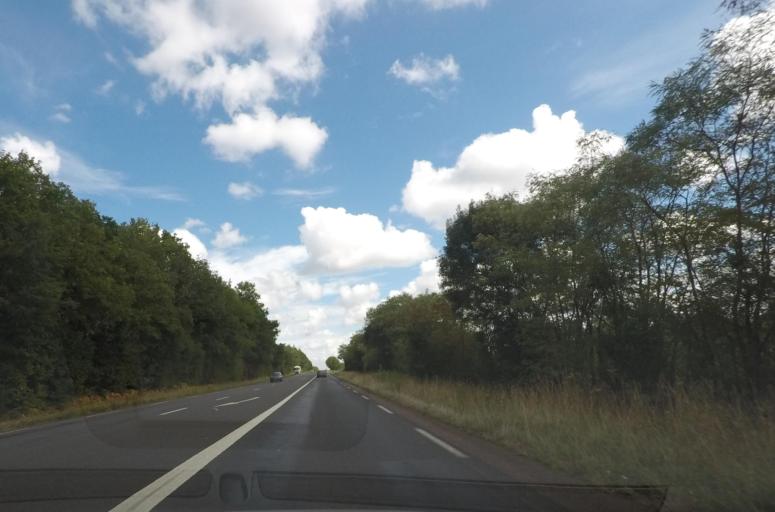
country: FR
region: Pays de la Loire
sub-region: Departement de la Sarthe
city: Clermont-Creans
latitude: 47.7570
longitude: 0.0110
